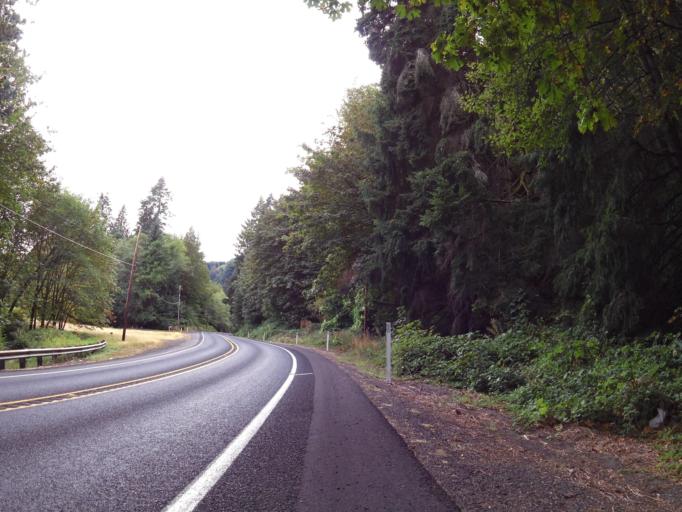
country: US
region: Oregon
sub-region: Columbia County
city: Clatskanie
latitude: 46.1738
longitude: -123.2269
